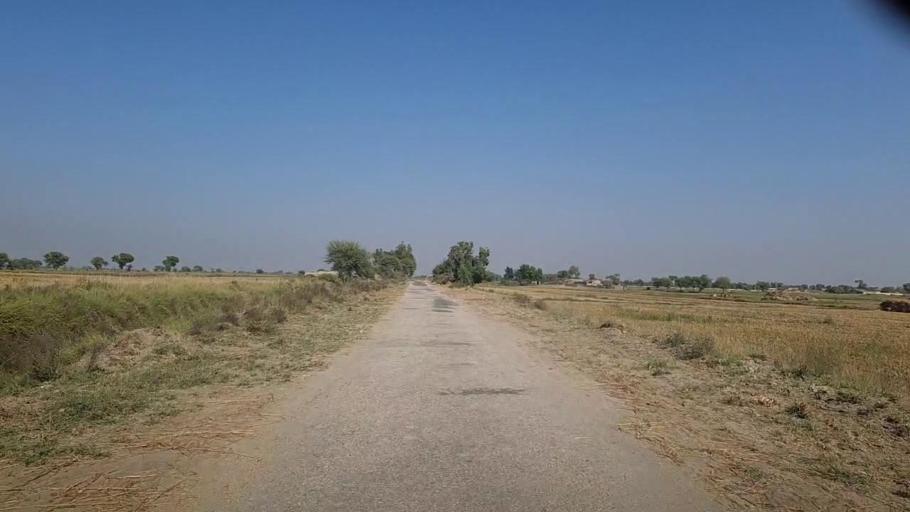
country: PK
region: Sindh
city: Tangwani
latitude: 28.2644
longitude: 68.9331
